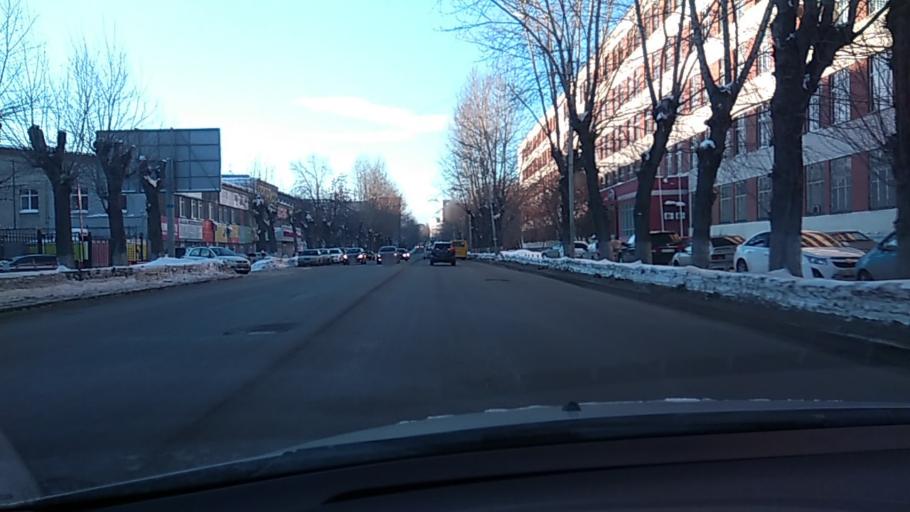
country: RU
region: Sverdlovsk
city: Yekaterinburg
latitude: 56.8243
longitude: 60.6494
